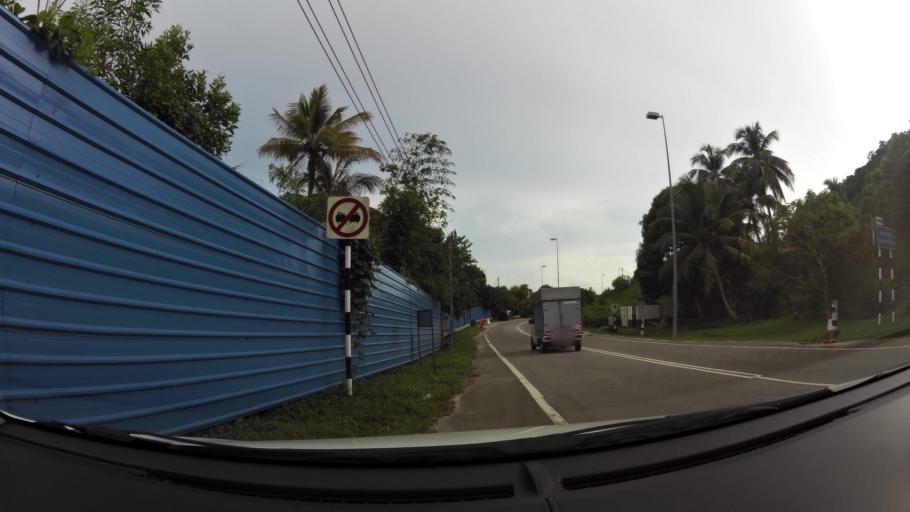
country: BN
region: Brunei and Muara
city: Bandar Seri Begawan
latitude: 4.9240
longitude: 115.0116
